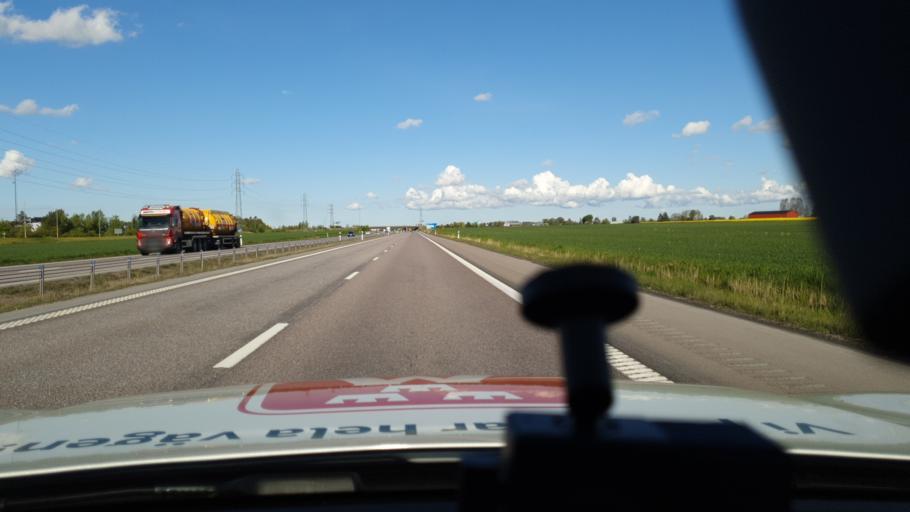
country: SE
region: OEstergoetland
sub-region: Linkopings Kommun
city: Linkoping
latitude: 58.4371
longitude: 15.5961
